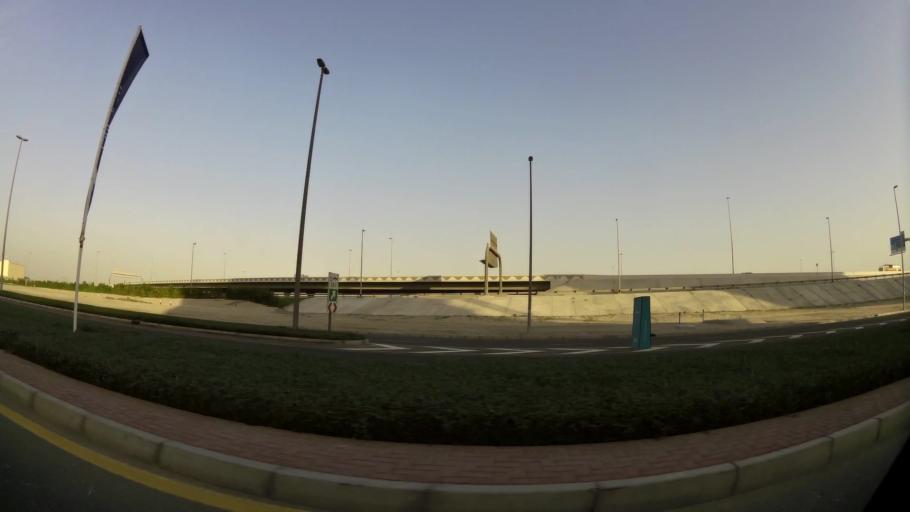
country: AE
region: Dubai
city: Dubai
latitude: 25.1830
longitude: 55.2841
